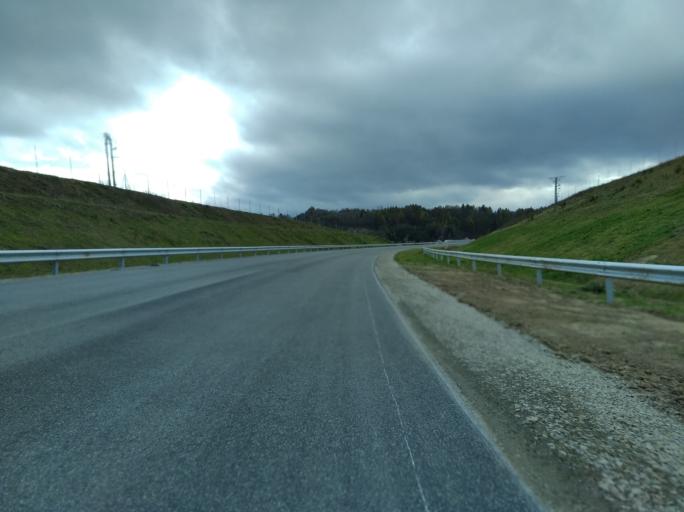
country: PL
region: Subcarpathian Voivodeship
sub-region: Powiat strzyzowski
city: Strzyzow
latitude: 49.8654
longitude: 21.8200
